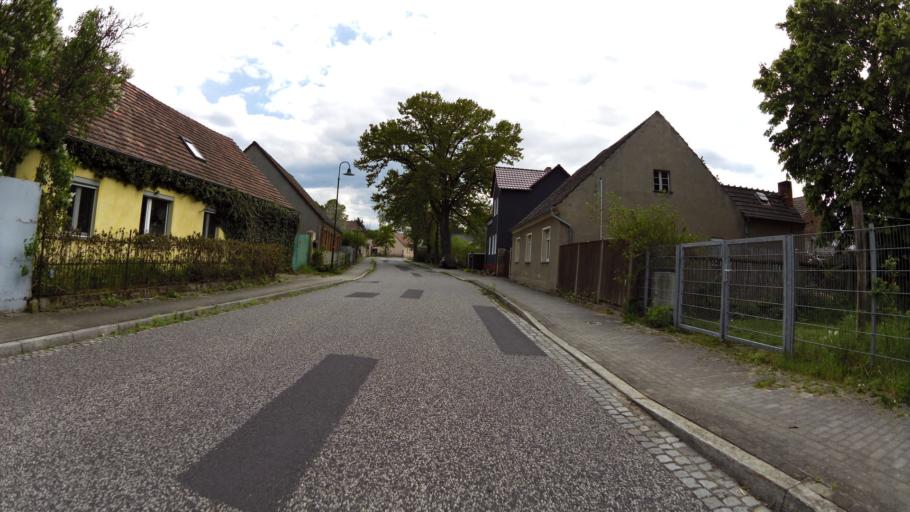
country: DE
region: Brandenburg
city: Rauen
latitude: 52.3313
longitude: 13.9517
